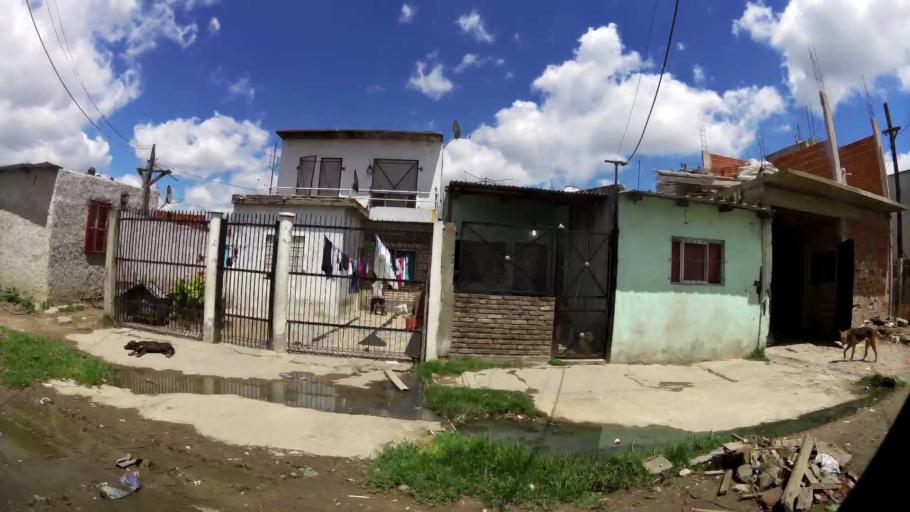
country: AR
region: Buenos Aires F.D.
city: Villa Lugano
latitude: -34.6888
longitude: -58.4449
